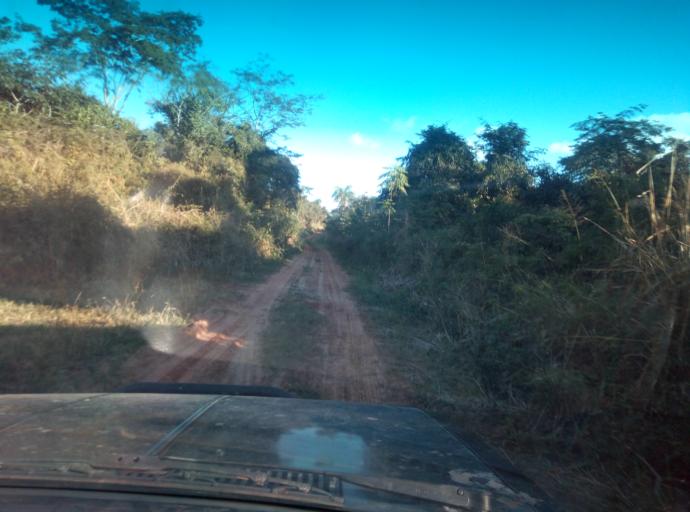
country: PY
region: Caaguazu
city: Carayao
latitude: -25.1840
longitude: -56.2624
